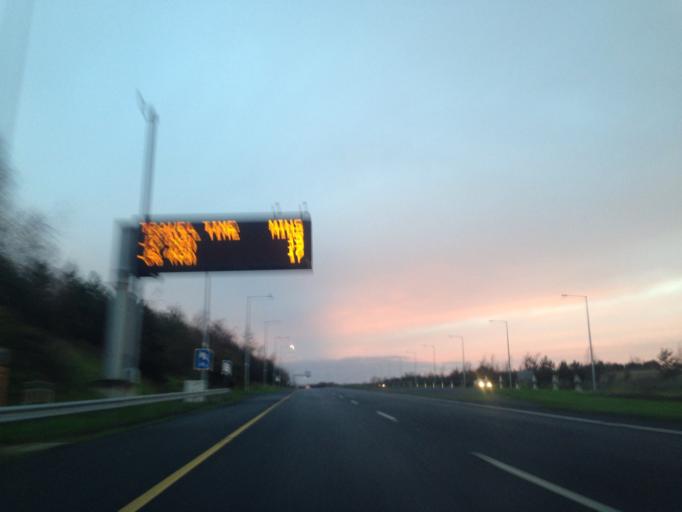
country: IE
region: Leinster
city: Loughlinstown
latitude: 53.2361
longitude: -6.1399
